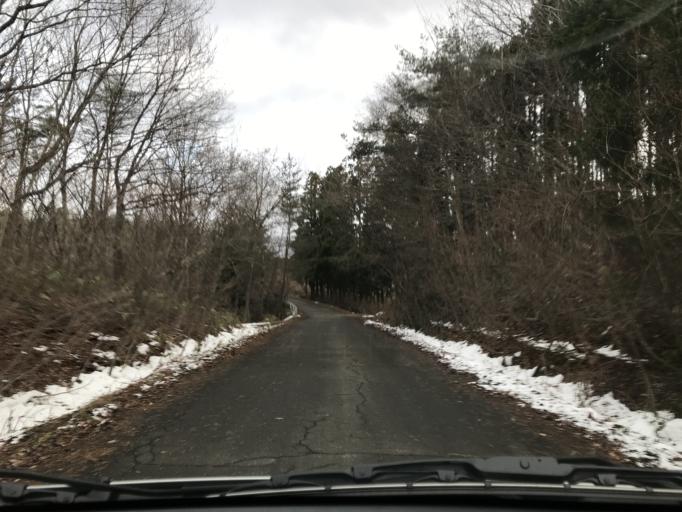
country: JP
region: Iwate
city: Ichinoseki
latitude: 38.9874
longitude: 141.0033
